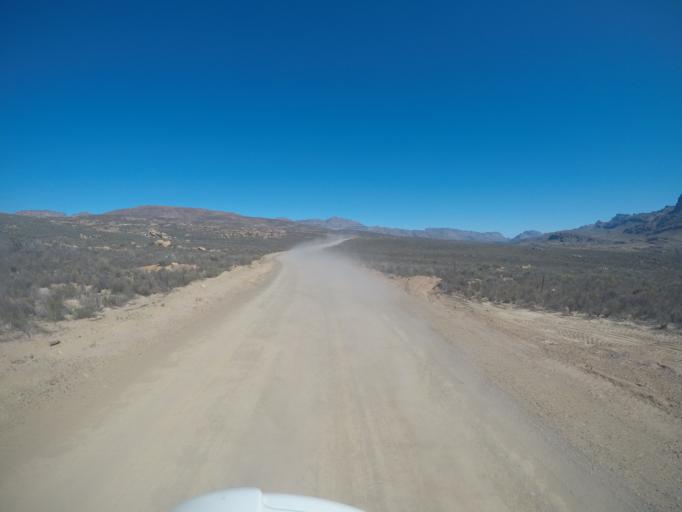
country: ZA
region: Western Cape
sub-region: West Coast District Municipality
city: Clanwilliam
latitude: -32.5053
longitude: 19.2952
